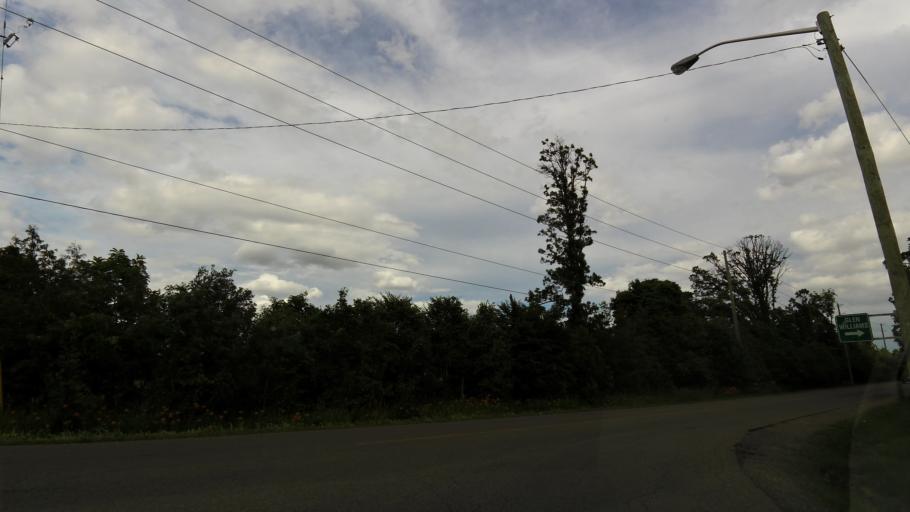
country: CA
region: Ontario
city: Brampton
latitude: 43.6779
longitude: -79.9166
